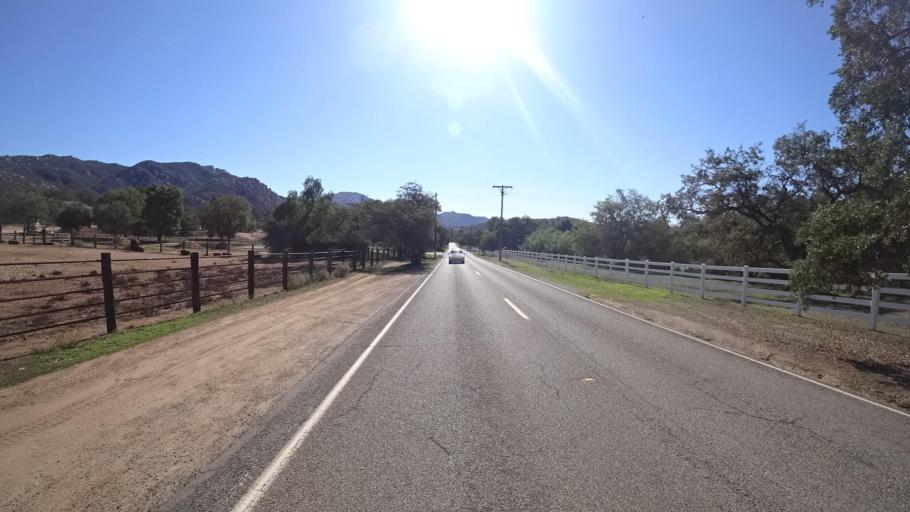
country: US
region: California
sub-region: San Diego County
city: Jamul
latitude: 32.7255
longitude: -116.8150
